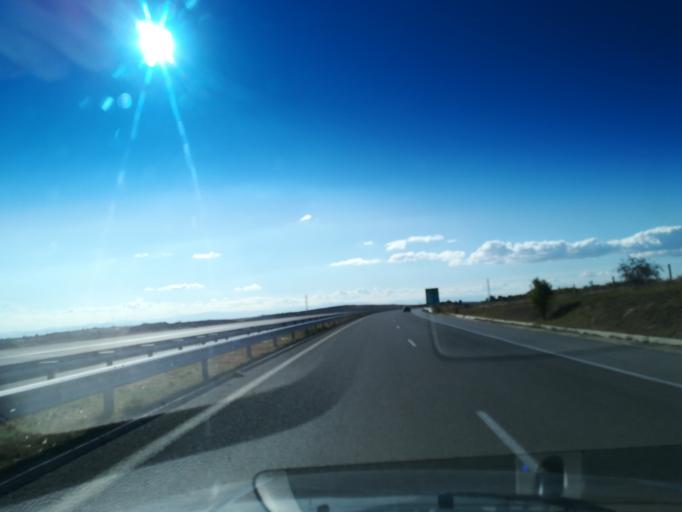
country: BG
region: Stara Zagora
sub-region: Obshtina Chirpan
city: Chirpan
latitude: 42.2543
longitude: 25.4246
